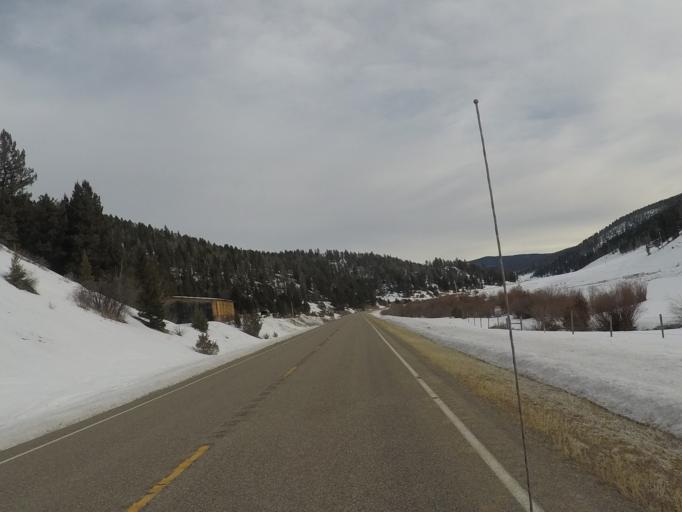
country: US
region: Montana
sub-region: Meagher County
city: White Sulphur Springs
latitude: 46.6878
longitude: -110.8730
